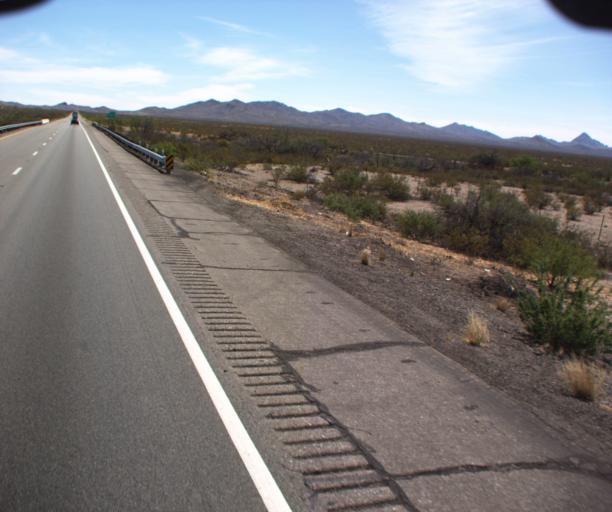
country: US
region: New Mexico
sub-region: Hidalgo County
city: Lordsburg
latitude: 32.2346
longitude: -109.0800
